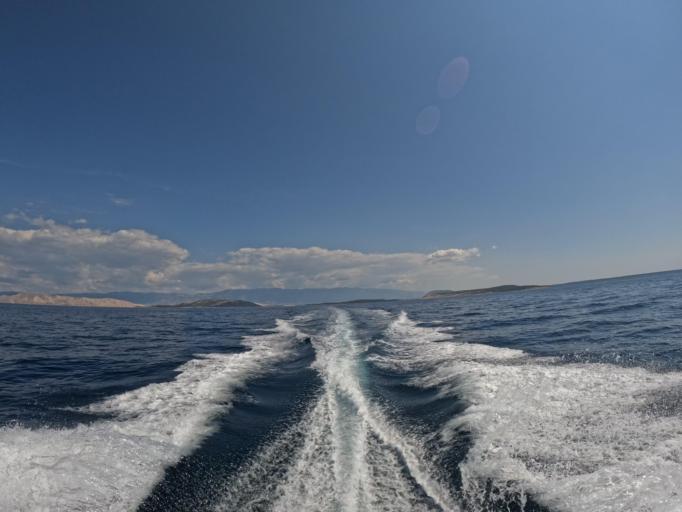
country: HR
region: Primorsko-Goranska
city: Lopar
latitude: 44.8758
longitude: 14.6614
